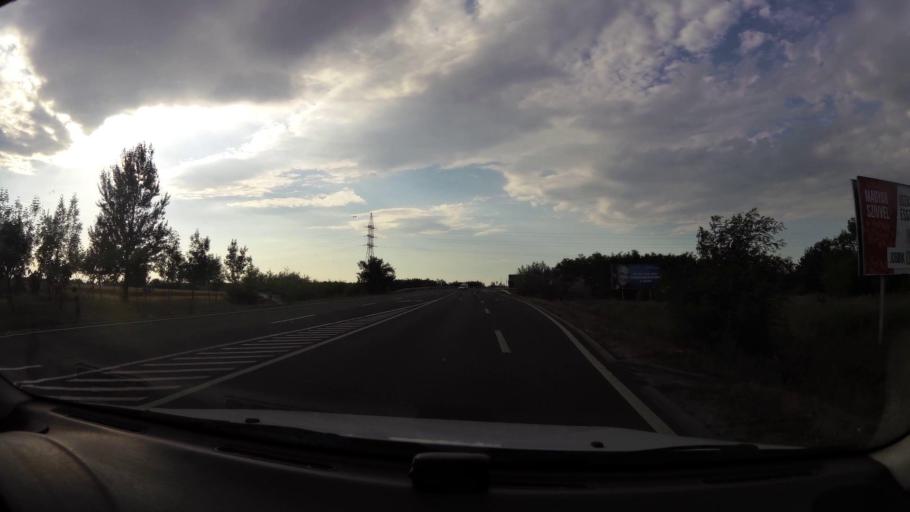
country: HU
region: Pest
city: Nagytarcsa
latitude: 47.5067
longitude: 19.2854
